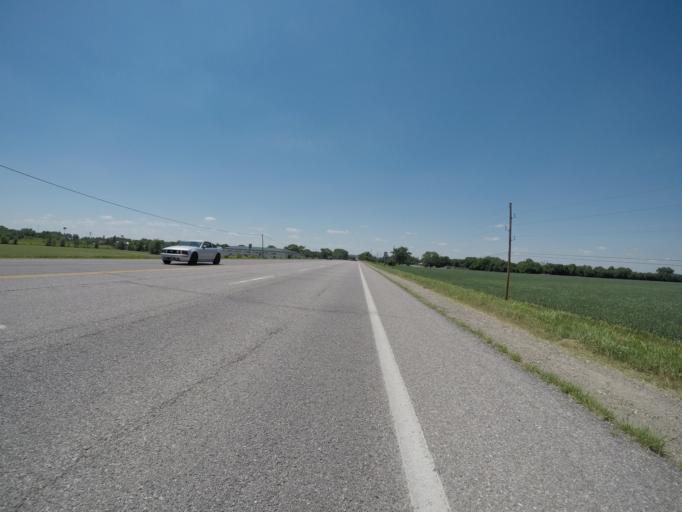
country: US
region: Kansas
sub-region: Geary County
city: Grandview Plaza
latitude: 39.0283
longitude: -96.8096
